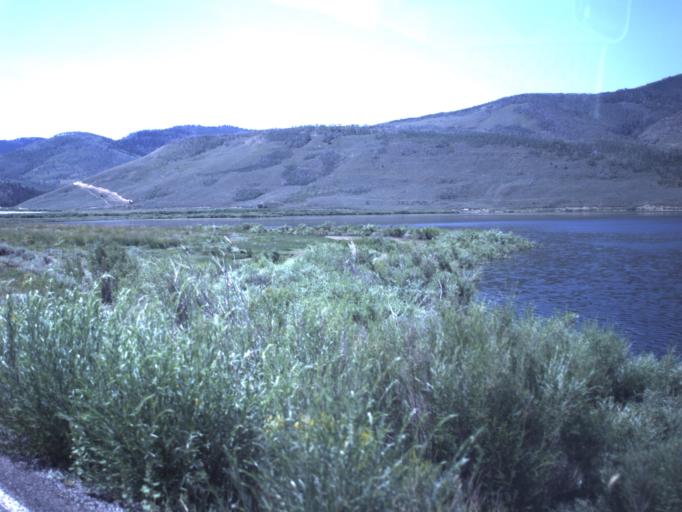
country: US
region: Utah
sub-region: Carbon County
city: Helper
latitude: 39.7518
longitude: -111.1499
